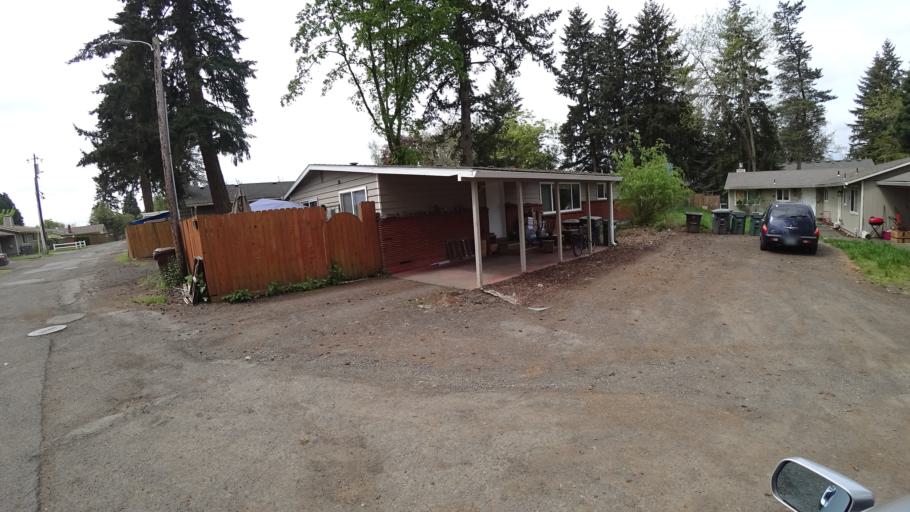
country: US
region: Oregon
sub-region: Washington County
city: Hillsboro
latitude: 45.5297
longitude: -122.9918
